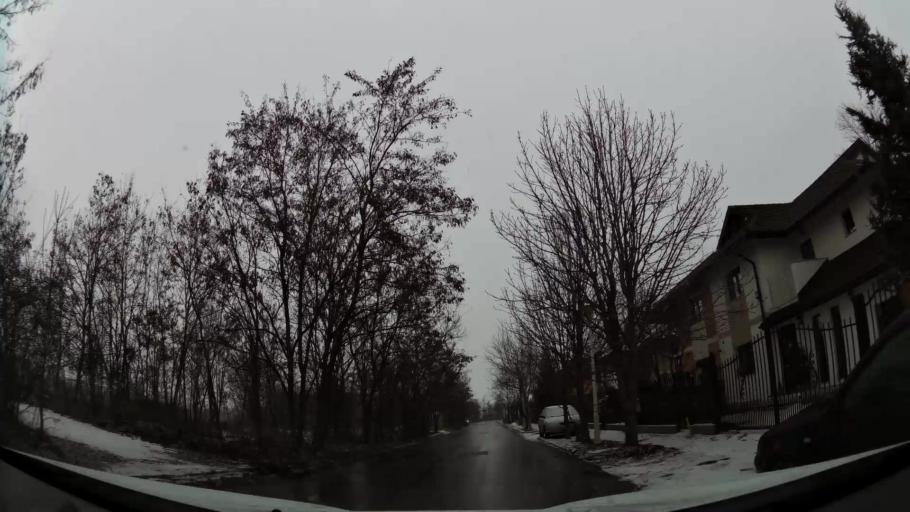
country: RO
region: Prahova
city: Ploiesti
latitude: 44.9595
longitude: 25.9976
